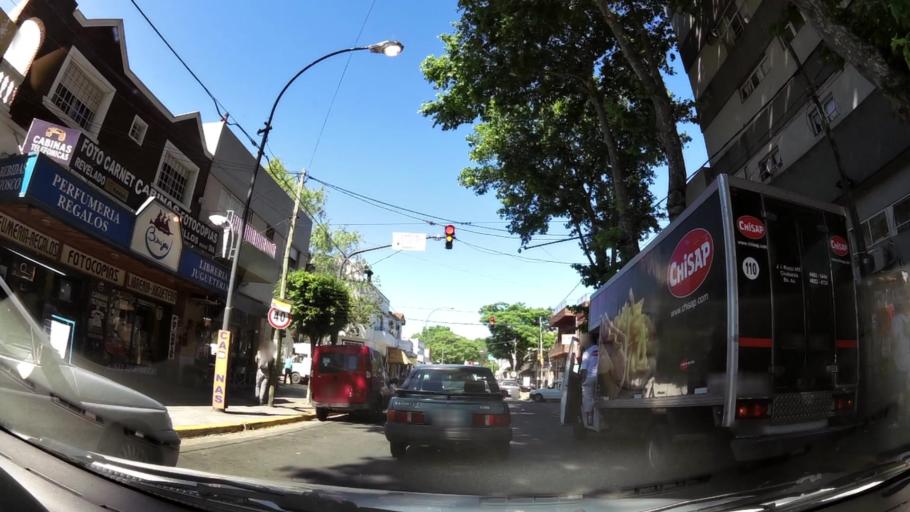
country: AR
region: Buenos Aires
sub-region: Partido de Vicente Lopez
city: Olivos
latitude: -34.5230
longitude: -58.4895
